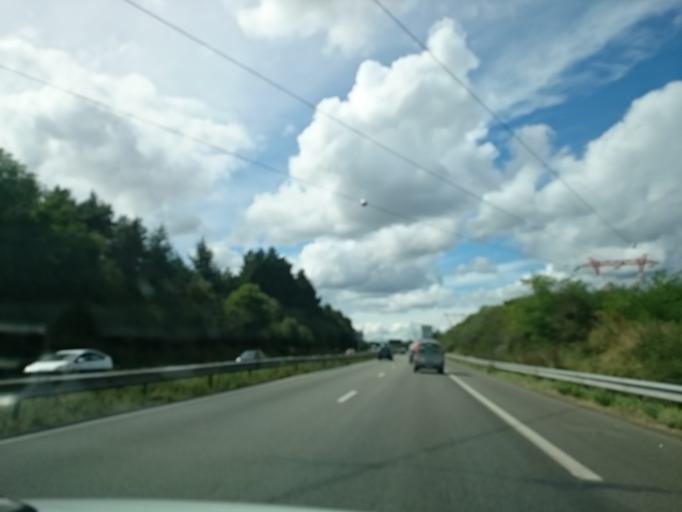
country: FR
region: Pays de la Loire
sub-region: Departement de la Loire-Atlantique
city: Bouguenais
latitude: 47.1758
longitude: -1.5970
